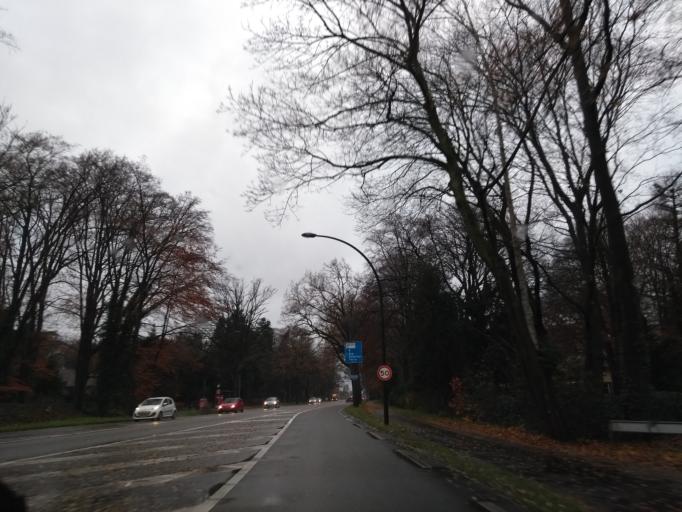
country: NL
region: Overijssel
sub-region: Gemeente Hengelo
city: Hengelo
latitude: 52.2539
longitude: 6.8170
